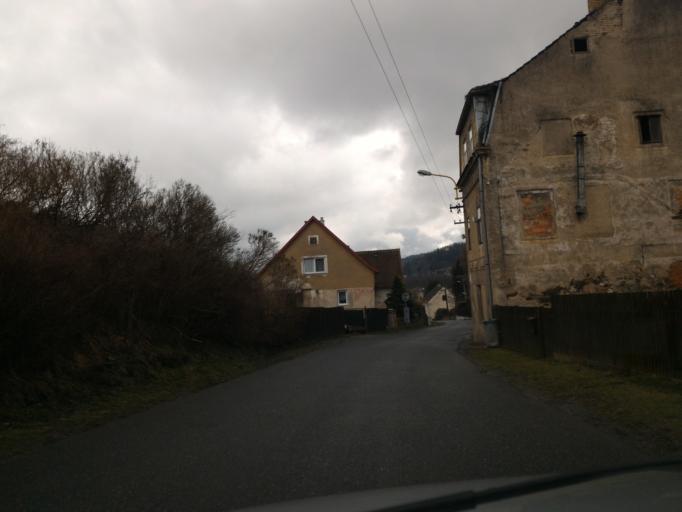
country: CZ
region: Liberecky
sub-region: Okres Liberec
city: Frydlant
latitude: 50.9259
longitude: 15.0740
